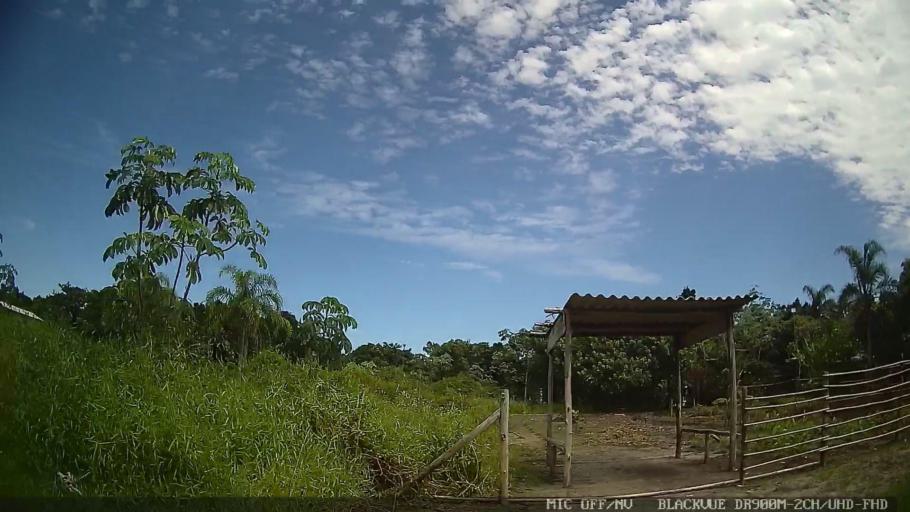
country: BR
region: Sao Paulo
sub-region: Iguape
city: Iguape
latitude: -24.7252
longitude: -47.5236
